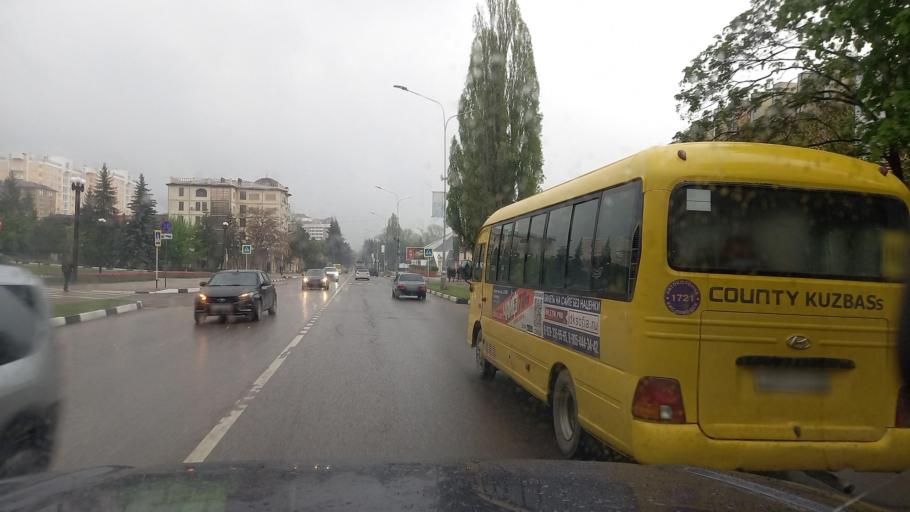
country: RU
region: Stavropol'skiy
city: Kislovodsk
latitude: 43.9114
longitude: 42.7182
